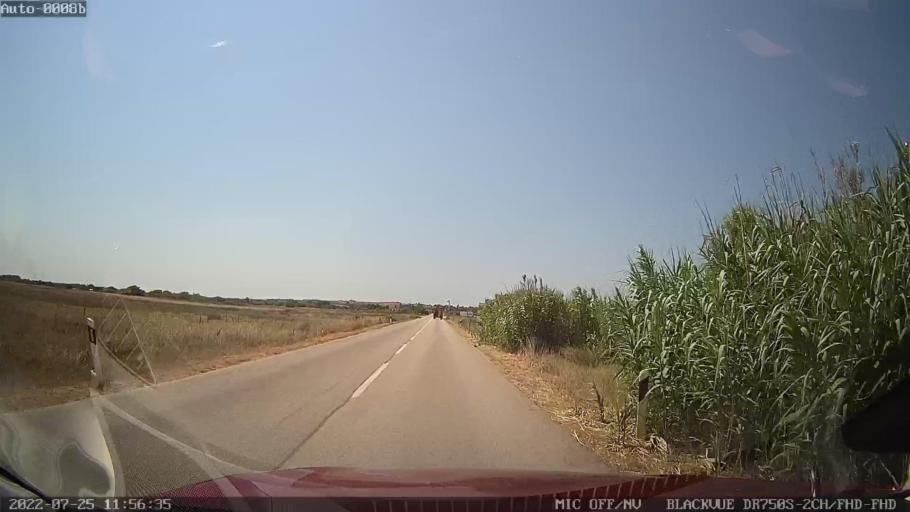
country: HR
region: Zadarska
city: Vrsi
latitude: 44.2485
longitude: 15.2171
